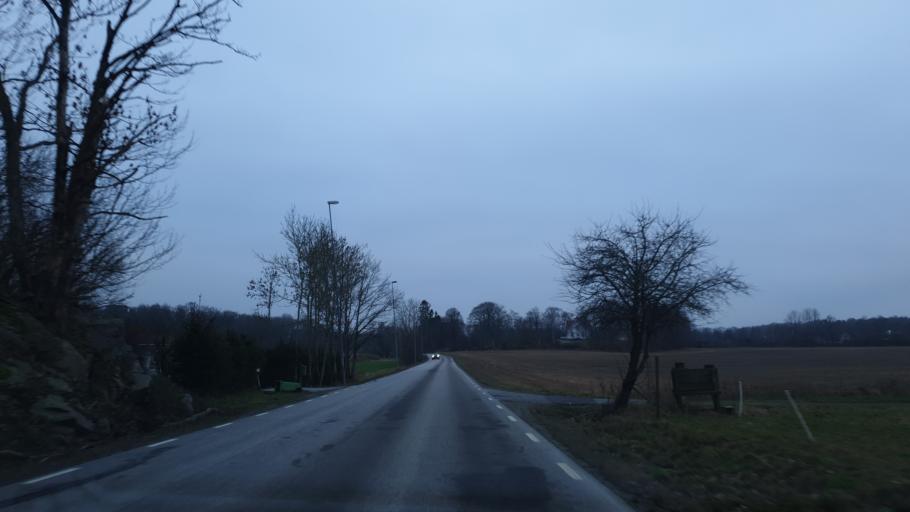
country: SE
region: Blekinge
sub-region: Karlskrona Kommun
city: Rodeby
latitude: 56.2142
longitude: 15.6660
